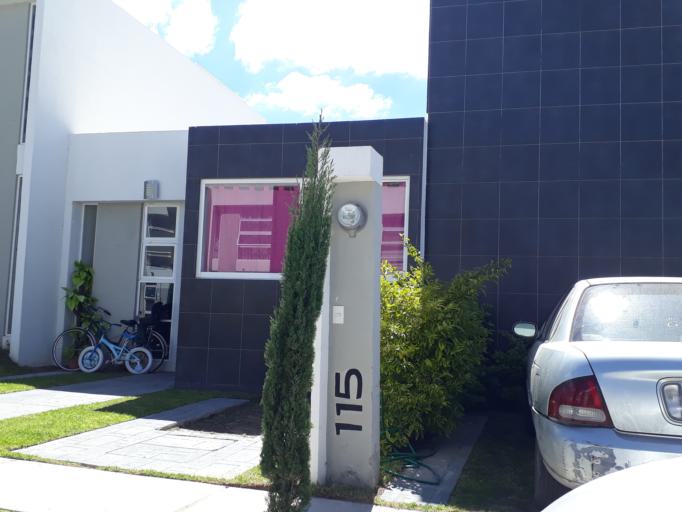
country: MX
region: Aguascalientes
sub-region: Aguascalientes
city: San Sebastian [Fraccionamiento]
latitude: 21.8307
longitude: -102.3006
